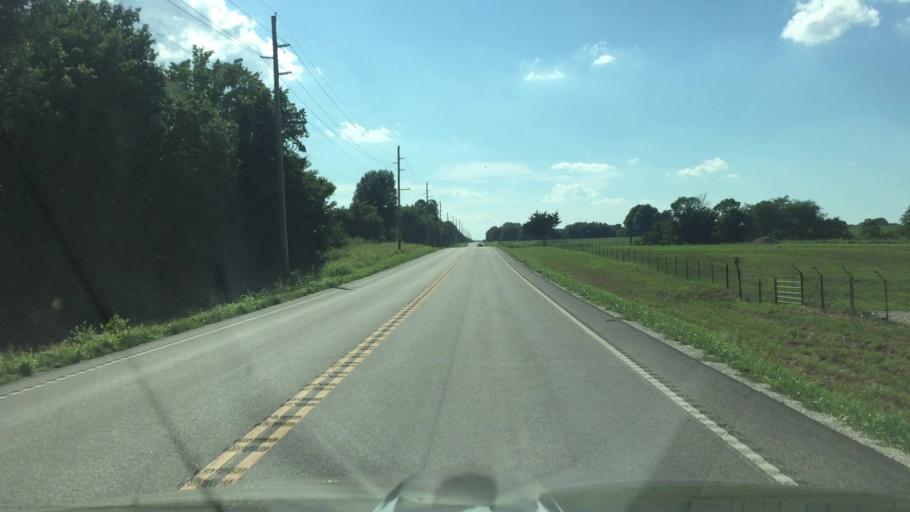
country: US
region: Missouri
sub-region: Morgan County
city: Versailles
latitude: 38.3958
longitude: -92.7223
